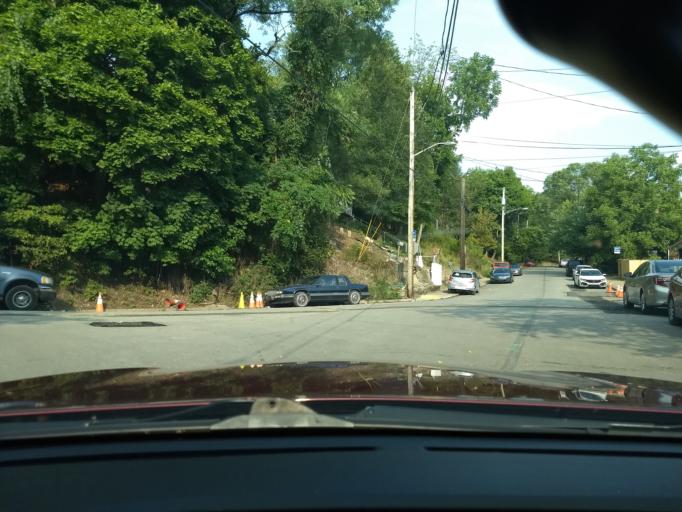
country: US
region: Pennsylvania
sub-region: Allegheny County
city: Wilkinsburg
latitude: 40.4620
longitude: -79.8940
